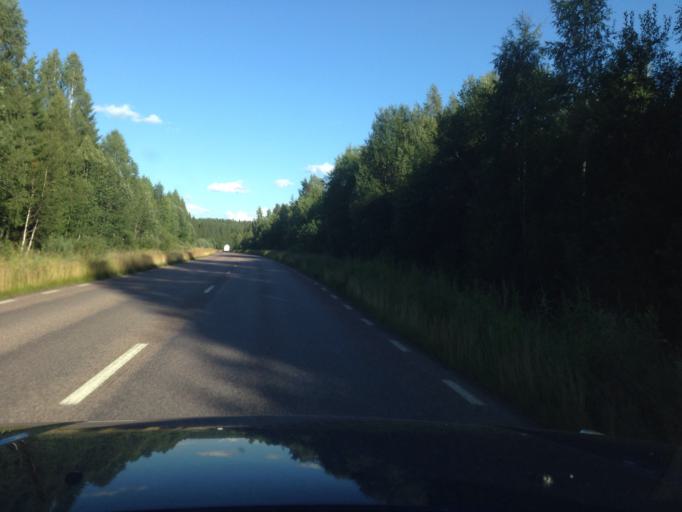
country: SE
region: Dalarna
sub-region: Ludvika Kommun
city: Ludvika
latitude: 60.1424
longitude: 15.1220
